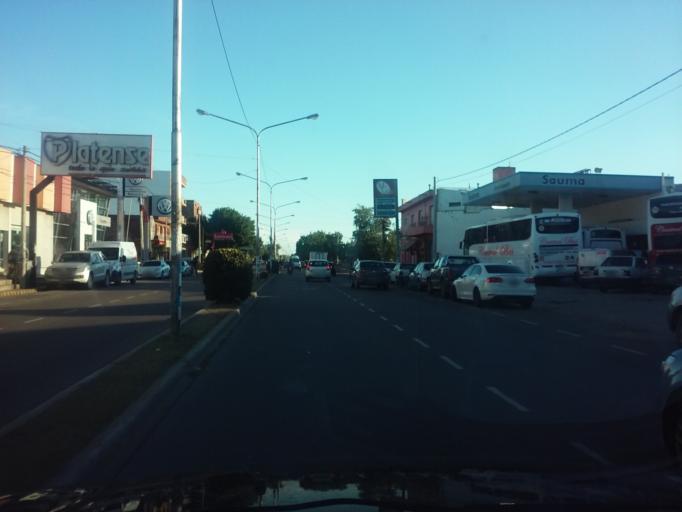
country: AR
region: La Pampa
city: Santa Rosa
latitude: -36.6258
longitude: -64.2815
